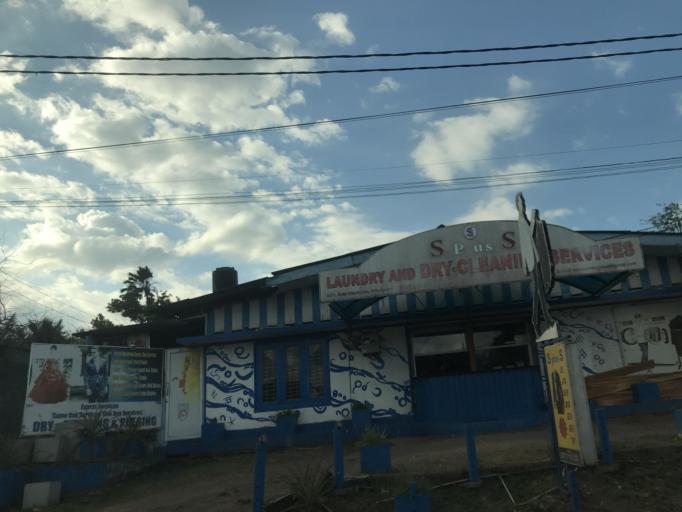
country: LK
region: Western
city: Gampaha
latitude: 7.0480
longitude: 80.0003
